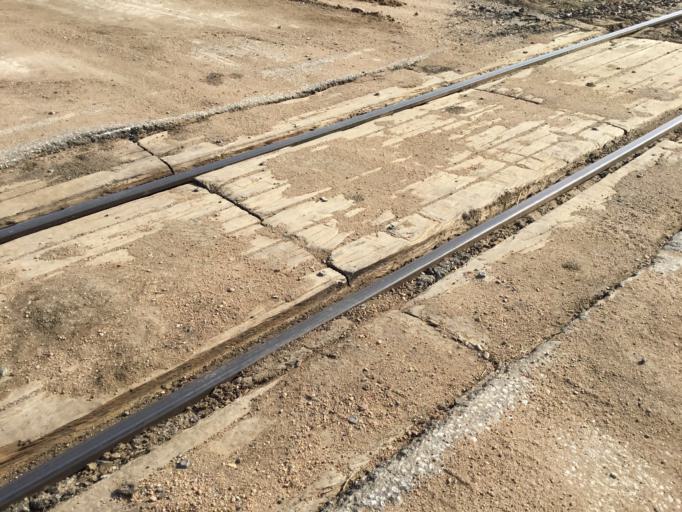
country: US
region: Kansas
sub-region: Ellsworth County
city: Ellsworth
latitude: 38.7301
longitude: -98.0398
